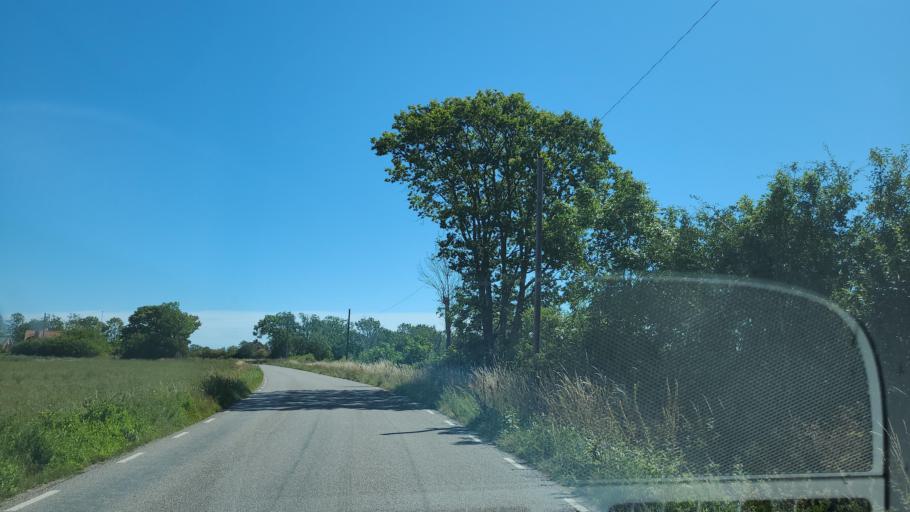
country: SE
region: Kalmar
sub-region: Borgholms Kommun
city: Borgholm
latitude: 56.7673
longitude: 16.5923
